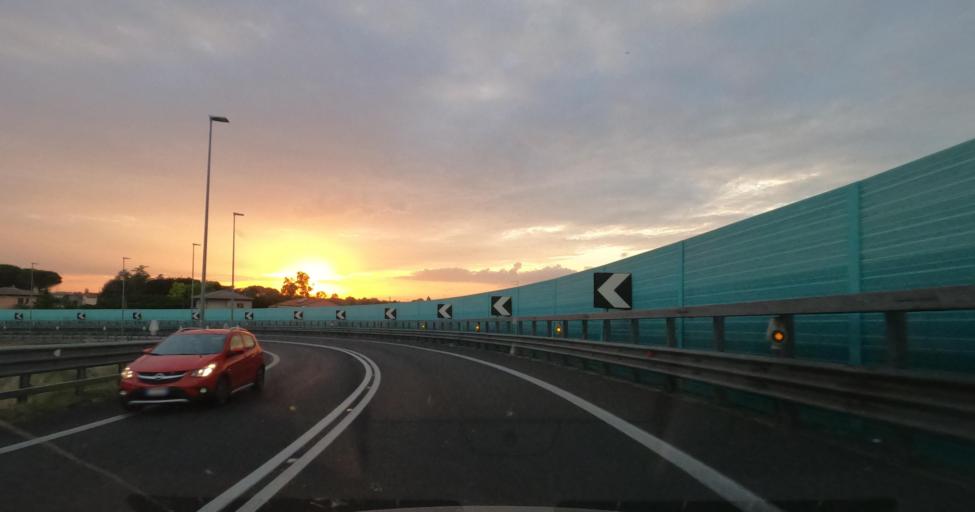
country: IT
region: Veneto
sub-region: Provincia di Venezia
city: Fornase
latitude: 45.4670
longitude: 12.1714
